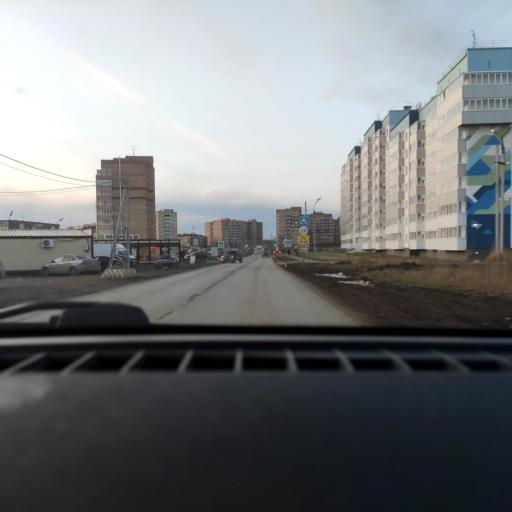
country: RU
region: Perm
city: Froly
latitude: 57.9197
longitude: 56.2799
